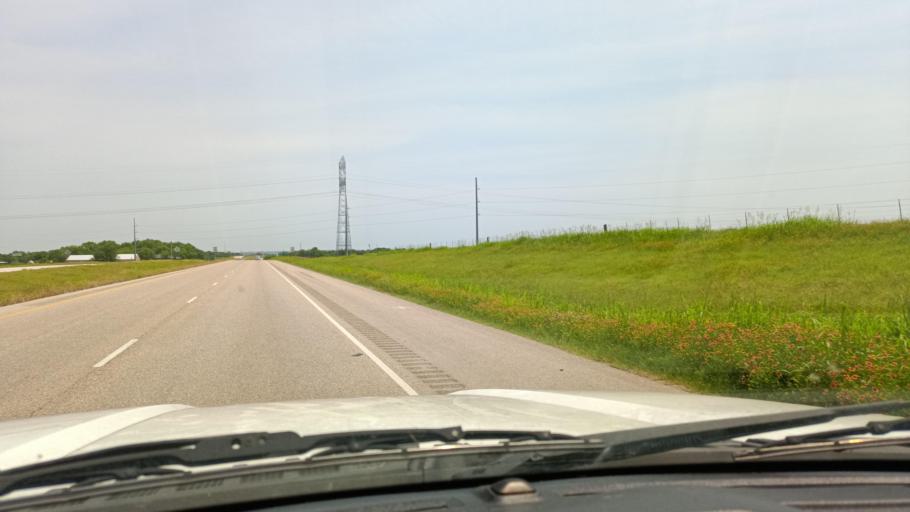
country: US
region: Texas
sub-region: Bell County
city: Temple
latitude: 31.0489
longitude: -97.3259
